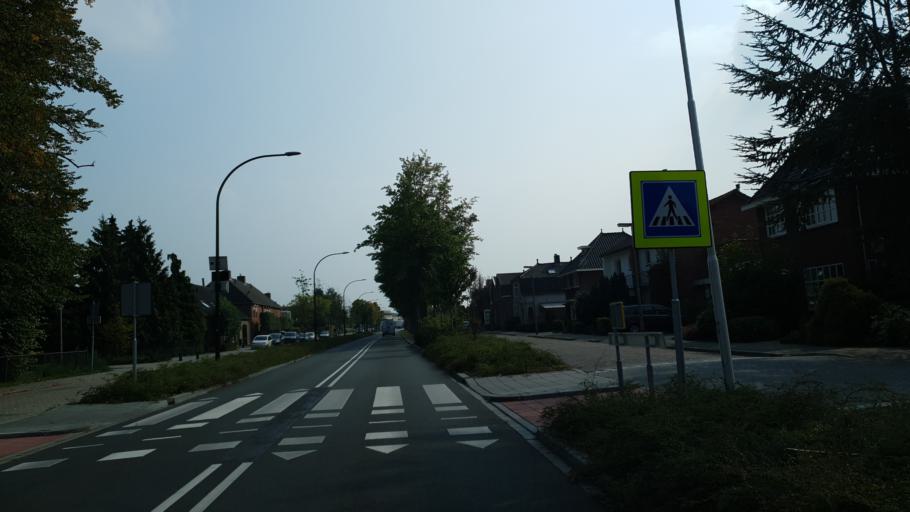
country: NL
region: North Brabant
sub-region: Gemeente Valkenswaard
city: Valkenswaard
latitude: 51.3469
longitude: 5.4659
